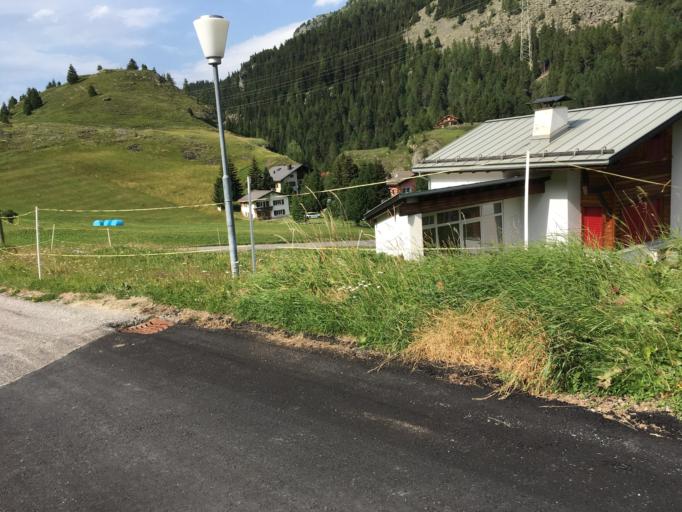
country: CH
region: Grisons
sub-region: Maloja District
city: Silvaplana
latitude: 46.4692
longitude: 9.6485
